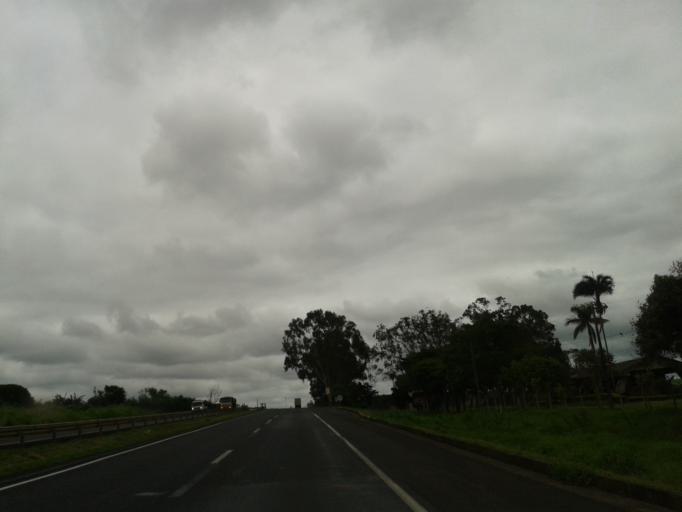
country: BR
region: Minas Gerais
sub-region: Uberlandia
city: Uberlandia
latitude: -18.9657
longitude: -48.2152
